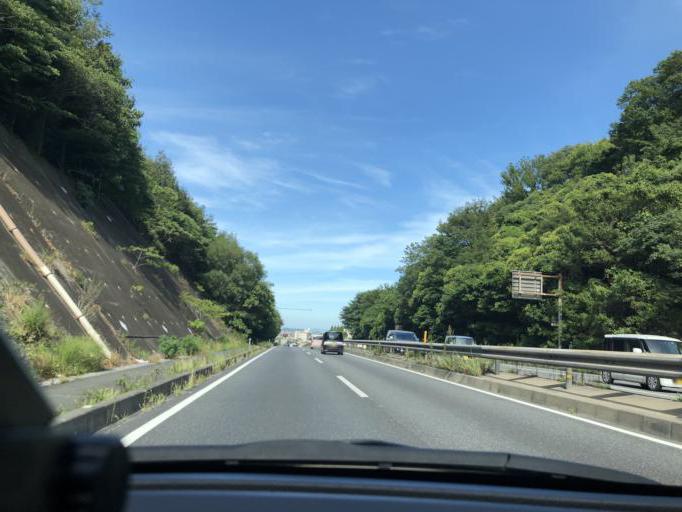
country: JP
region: Okayama
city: Kurashiki
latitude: 34.5850
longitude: 133.7862
